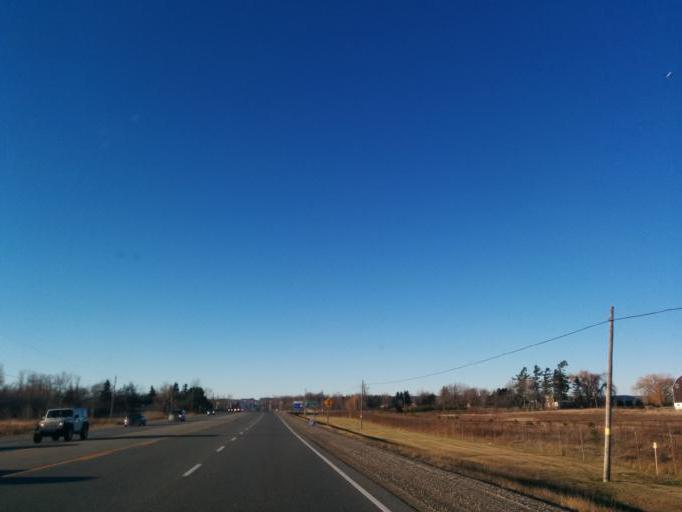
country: CA
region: Ontario
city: Brampton
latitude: 43.7980
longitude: -79.9115
